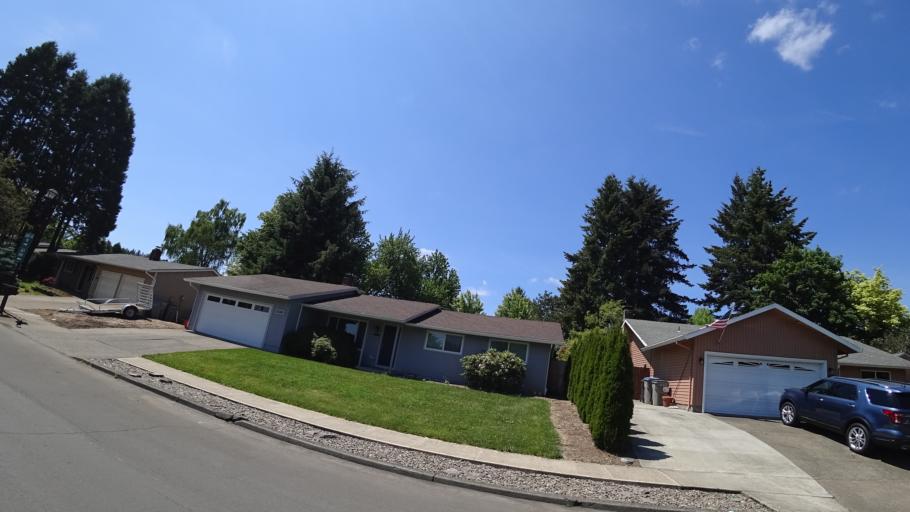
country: US
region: Oregon
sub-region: Washington County
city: King City
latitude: 45.4314
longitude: -122.8071
